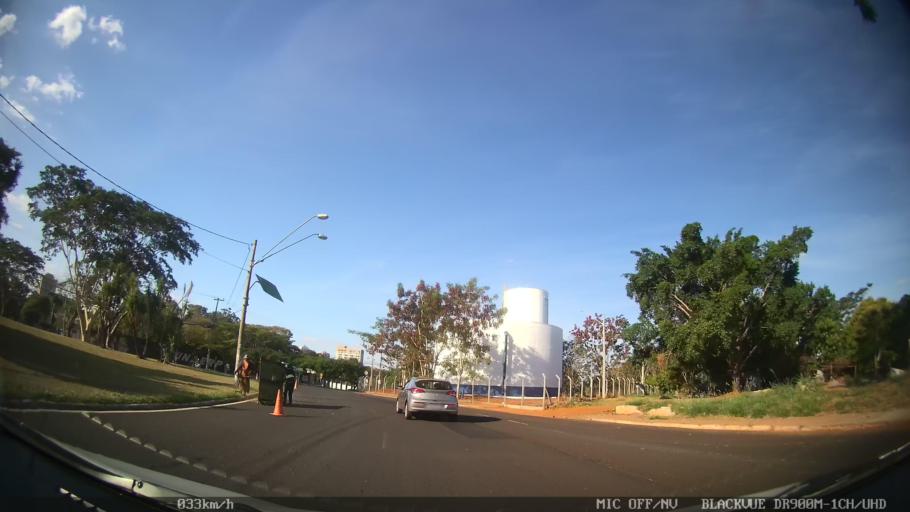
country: BR
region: Sao Paulo
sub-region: Ribeirao Preto
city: Ribeirao Preto
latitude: -21.2034
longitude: -47.7813
